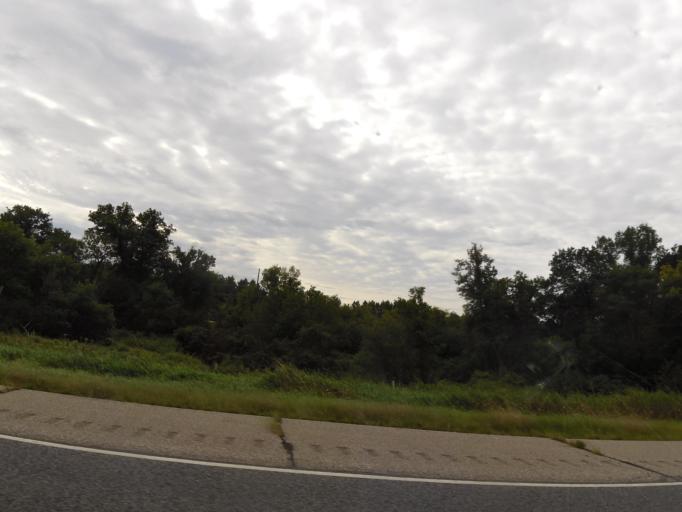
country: US
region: Wisconsin
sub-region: Monroe County
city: Sparta
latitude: 43.9431
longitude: -90.6841
